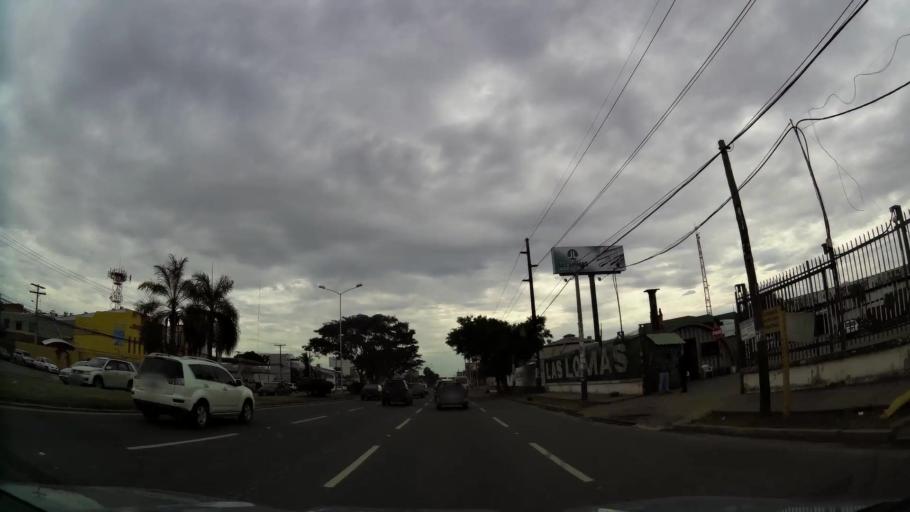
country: BO
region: Santa Cruz
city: Santa Cruz de la Sierra
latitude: -17.7559
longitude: -63.1776
